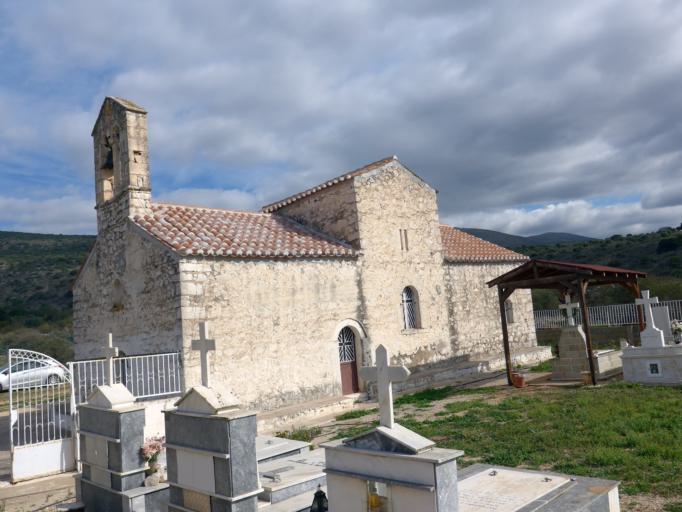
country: GR
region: Peloponnese
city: Asklipieio
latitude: 37.5076
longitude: 23.0127
